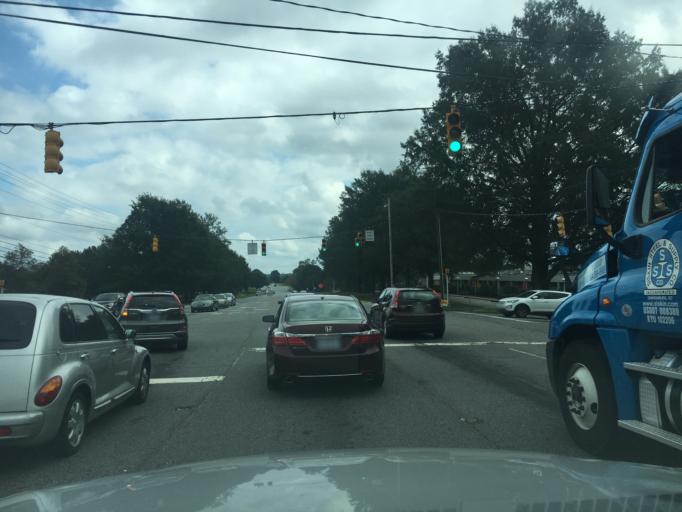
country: US
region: North Carolina
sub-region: Catawba County
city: Hickory
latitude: 35.7010
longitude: -81.2895
